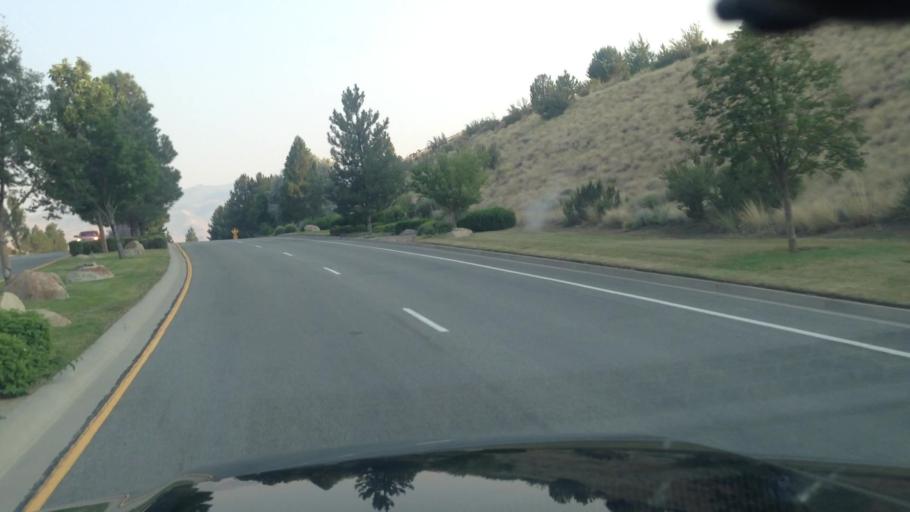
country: US
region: Nevada
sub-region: Washoe County
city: Mogul
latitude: 39.5262
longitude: -119.9118
